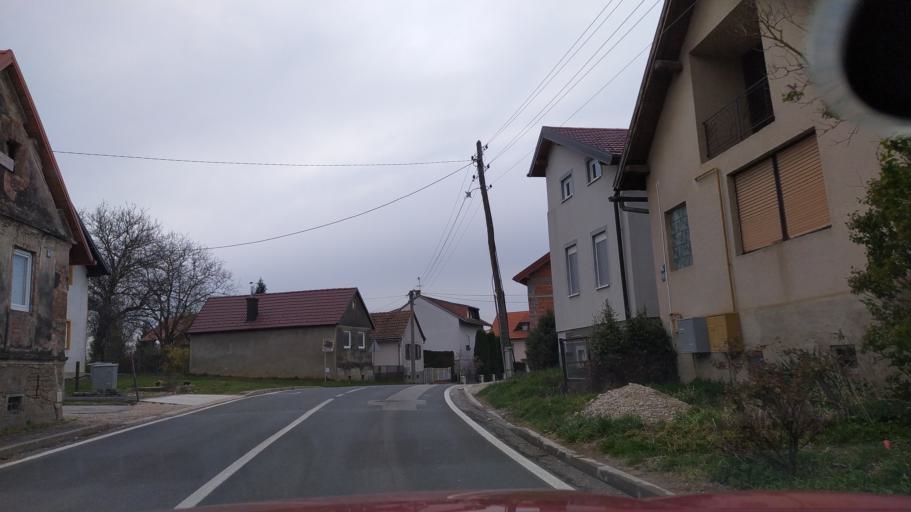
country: HR
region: Varazdinska
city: Jalzabet
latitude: 46.2084
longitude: 16.4530
